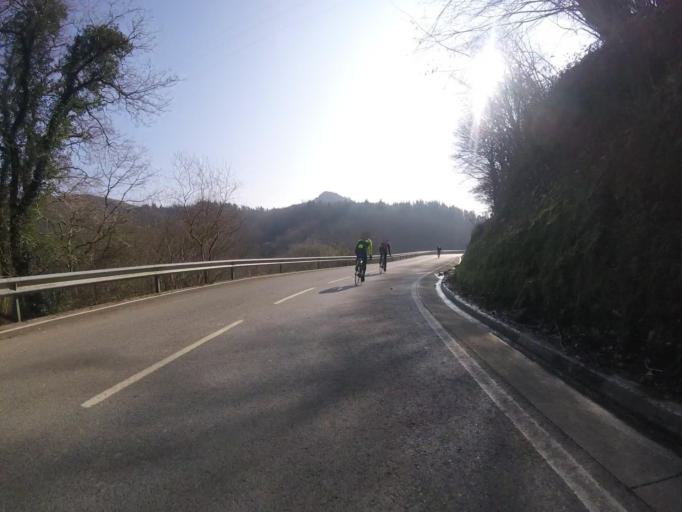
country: ES
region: Navarre
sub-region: Provincia de Navarra
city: Bera
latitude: 43.3057
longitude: -1.6892
